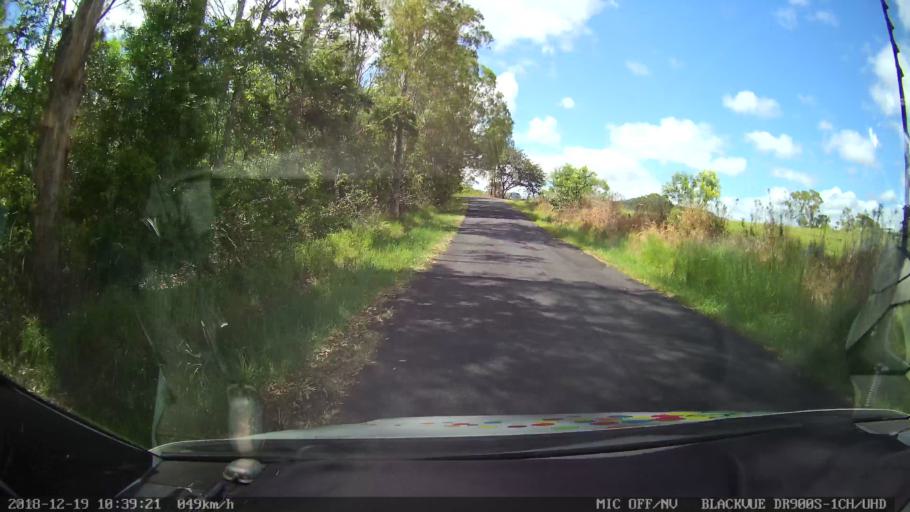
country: AU
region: New South Wales
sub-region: Lismore Municipality
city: Nimbin
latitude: -28.5800
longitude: 153.1546
